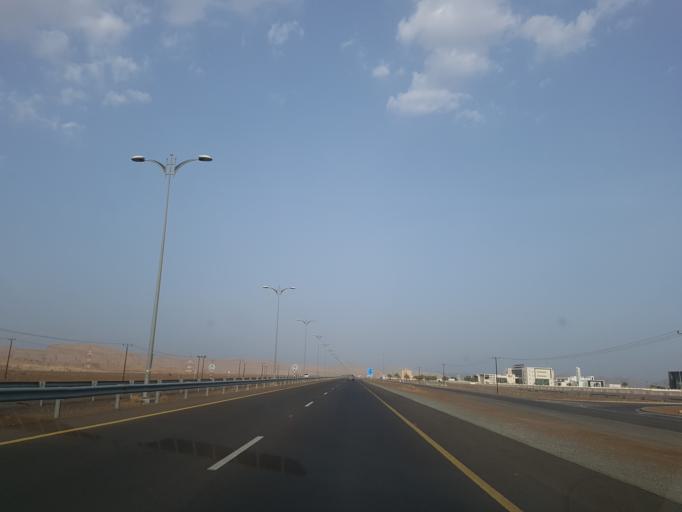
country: OM
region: Al Buraimi
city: Al Buraymi
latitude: 24.2380
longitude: 55.8905
